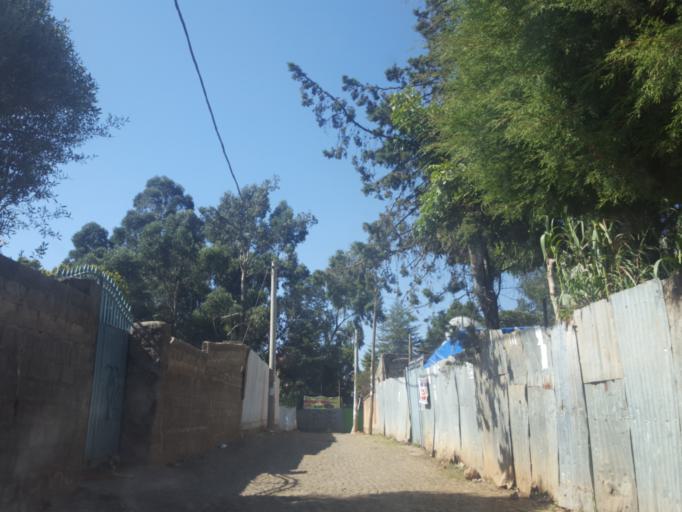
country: ET
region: Adis Abeba
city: Addis Ababa
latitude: 9.0549
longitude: 38.7367
